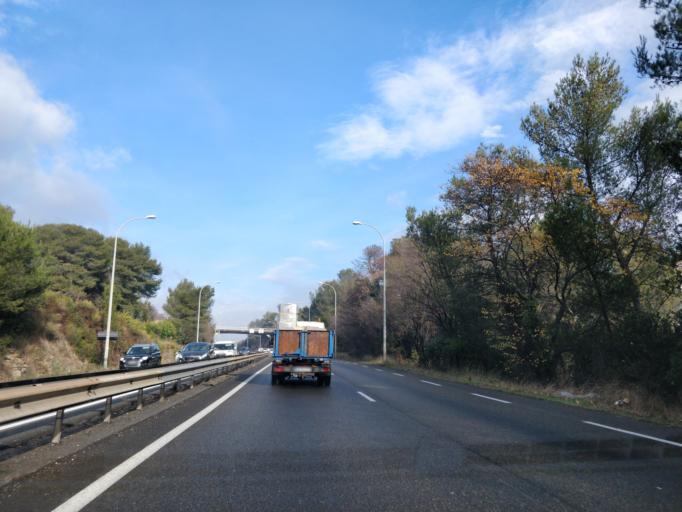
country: FR
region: Languedoc-Roussillon
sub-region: Departement du Gard
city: Nimes
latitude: 43.8333
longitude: 4.3220
